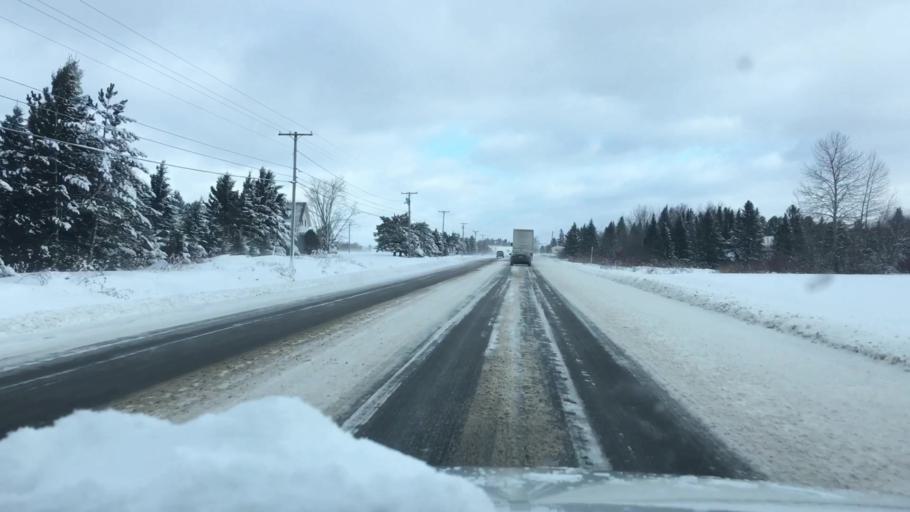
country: US
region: Maine
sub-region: Aroostook County
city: Presque Isle
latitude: 46.7365
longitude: -67.9992
